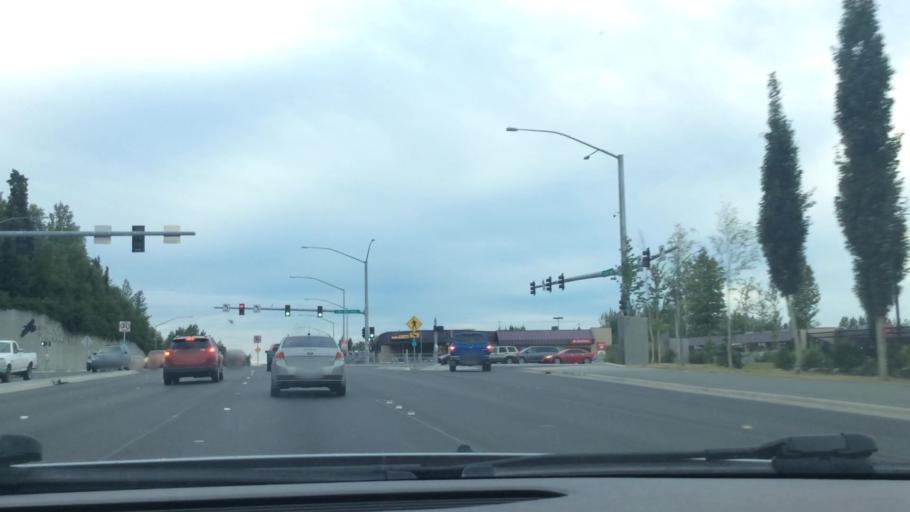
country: US
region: Alaska
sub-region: Anchorage Municipality
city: Anchorage
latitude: 61.1809
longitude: -149.8367
